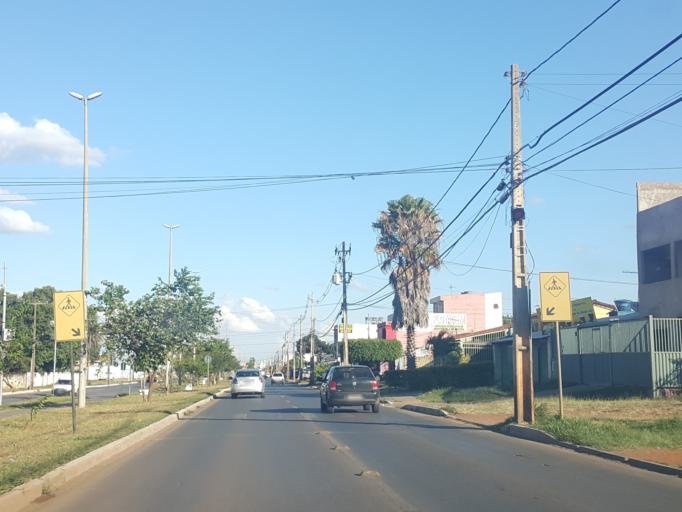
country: BR
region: Federal District
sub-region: Brasilia
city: Brasilia
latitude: -15.8240
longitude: -48.0939
